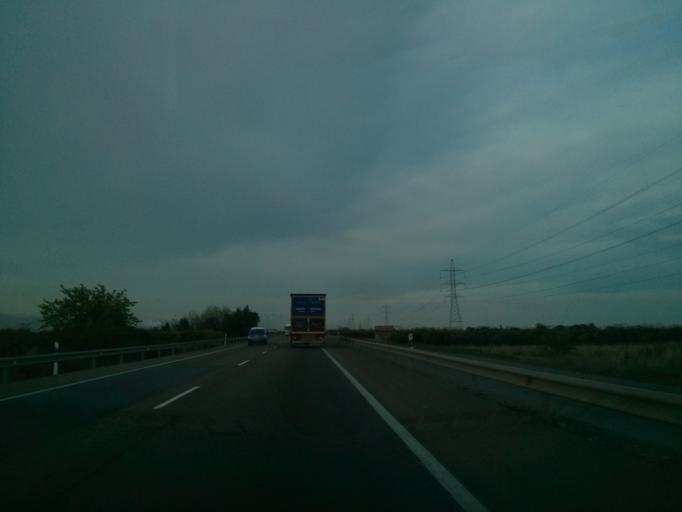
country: ES
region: Valencia
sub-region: Provincia de Castello
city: Vila-real
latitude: 39.9347
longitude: -0.0902
